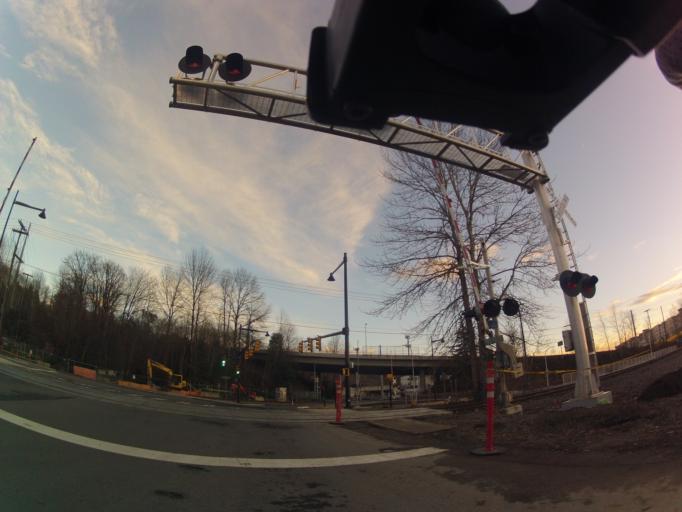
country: US
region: Washington
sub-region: King County
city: Renton
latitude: 47.5032
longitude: -122.2002
